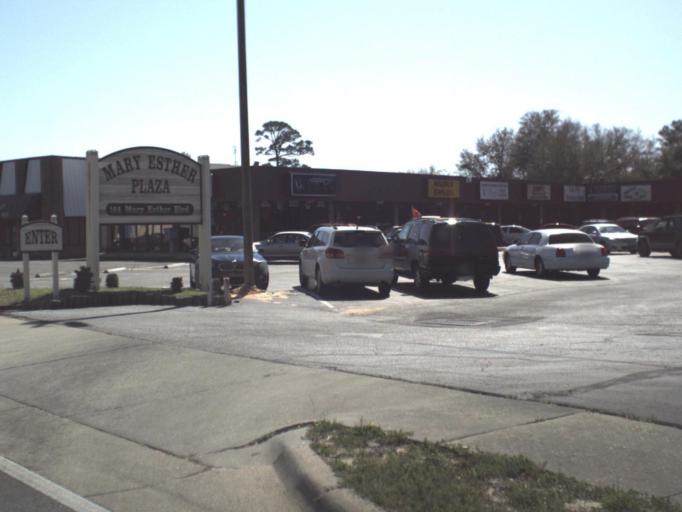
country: US
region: Florida
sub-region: Okaloosa County
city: Mary Esther
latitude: 30.4118
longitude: -86.6552
